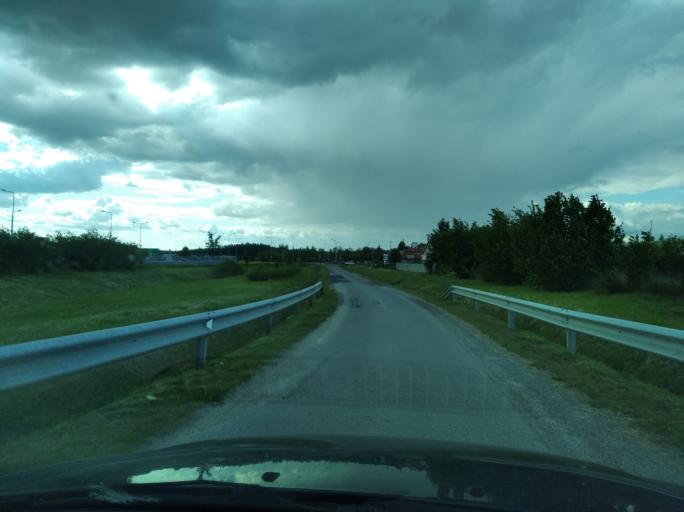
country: PL
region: Subcarpathian Voivodeship
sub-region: Powiat jaroslawski
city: Pawlosiow
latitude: 49.9762
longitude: 22.6447
